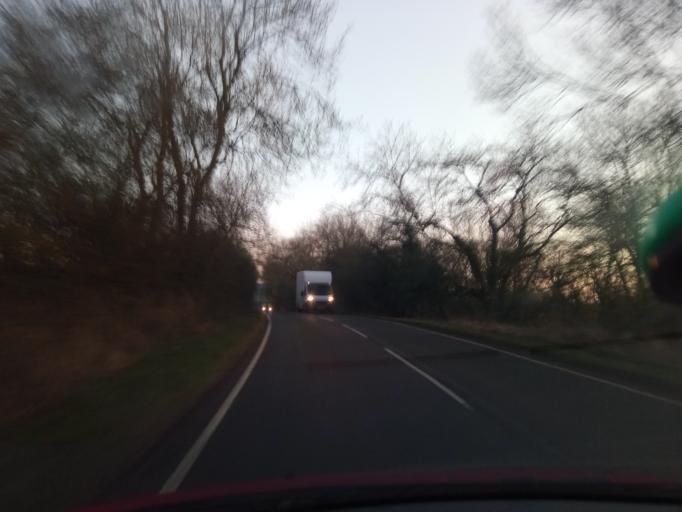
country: GB
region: England
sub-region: Leicestershire
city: Sileby
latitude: 52.7575
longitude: -1.0991
